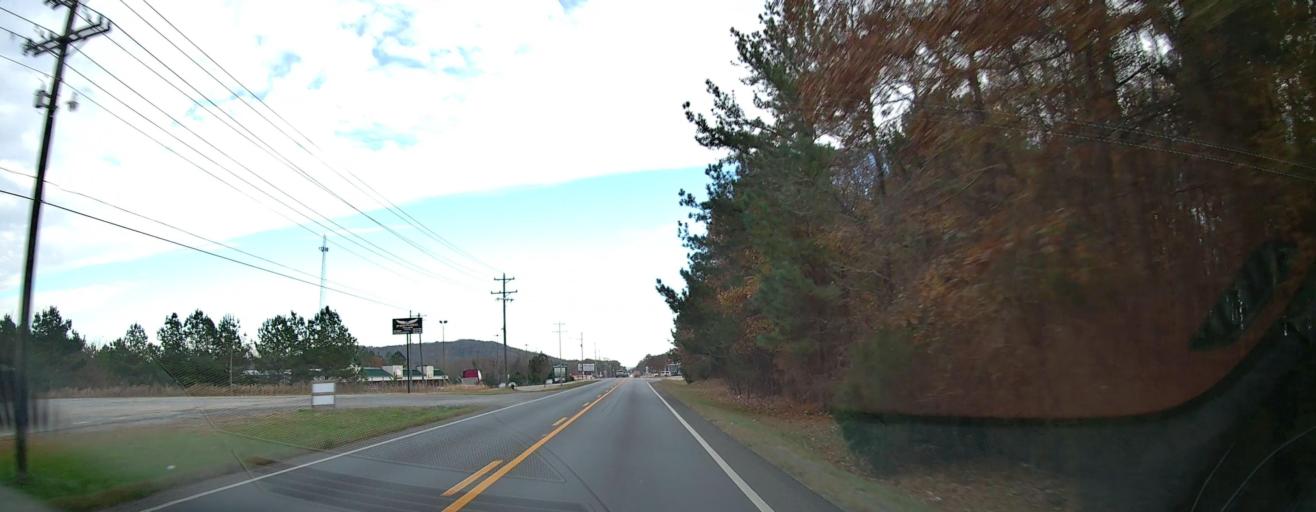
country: US
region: Alabama
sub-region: Morgan County
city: Priceville
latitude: 34.4482
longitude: -86.7596
